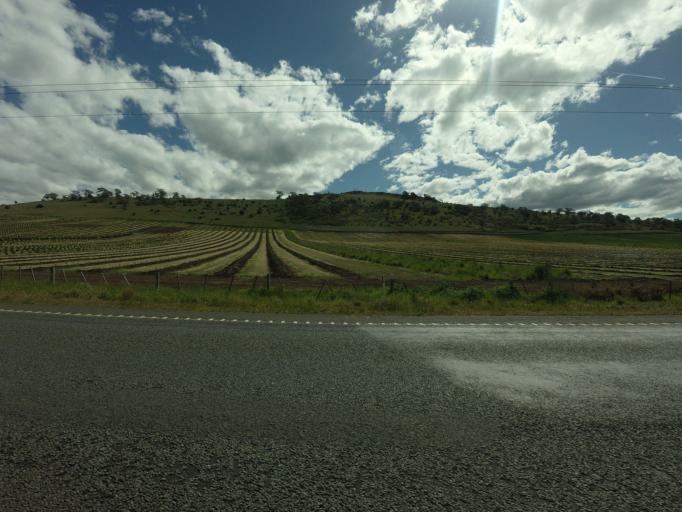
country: AU
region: Tasmania
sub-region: Northern Midlands
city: Evandale
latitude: -42.0526
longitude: 147.4823
